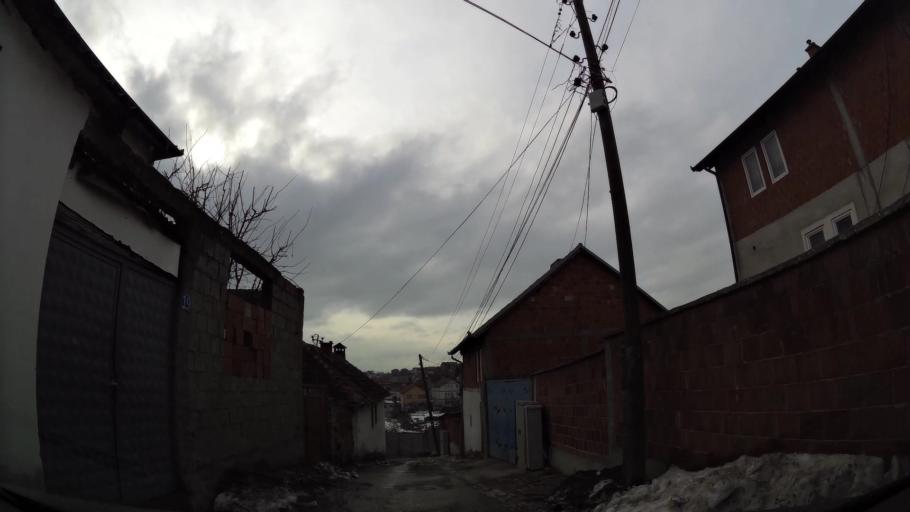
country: XK
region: Pristina
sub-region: Komuna e Prishtines
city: Pristina
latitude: 42.6759
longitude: 21.1616
